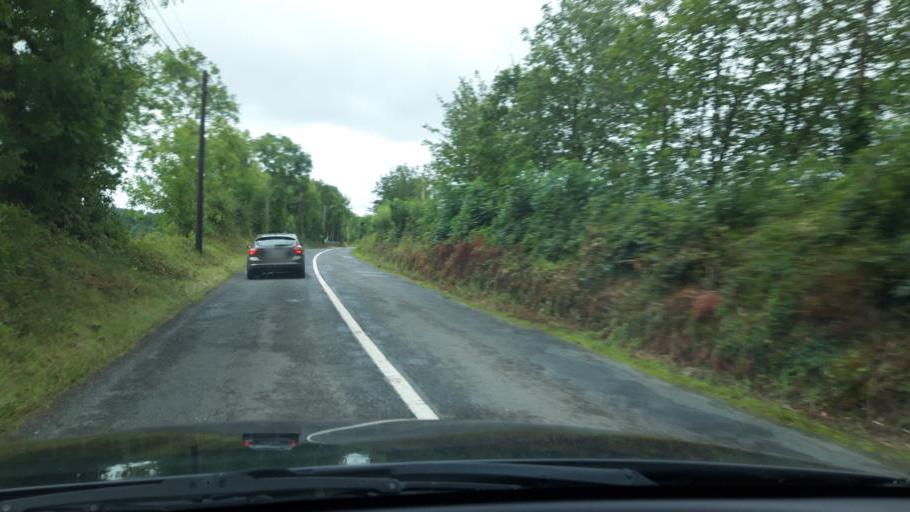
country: IE
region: Munster
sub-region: County Cork
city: Youghal
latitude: 52.1596
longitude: -7.8443
